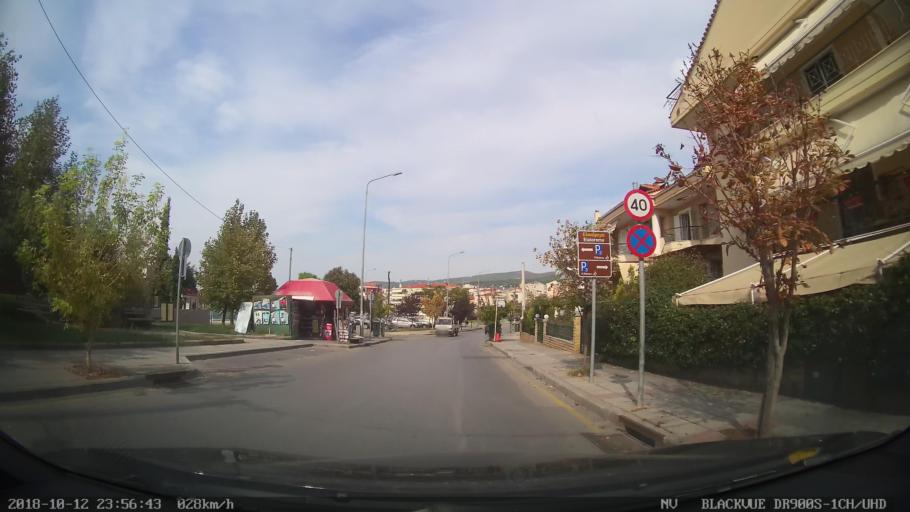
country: GR
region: Central Macedonia
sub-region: Nomos Thessalonikis
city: Pylaia
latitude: 40.6029
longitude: 22.9894
